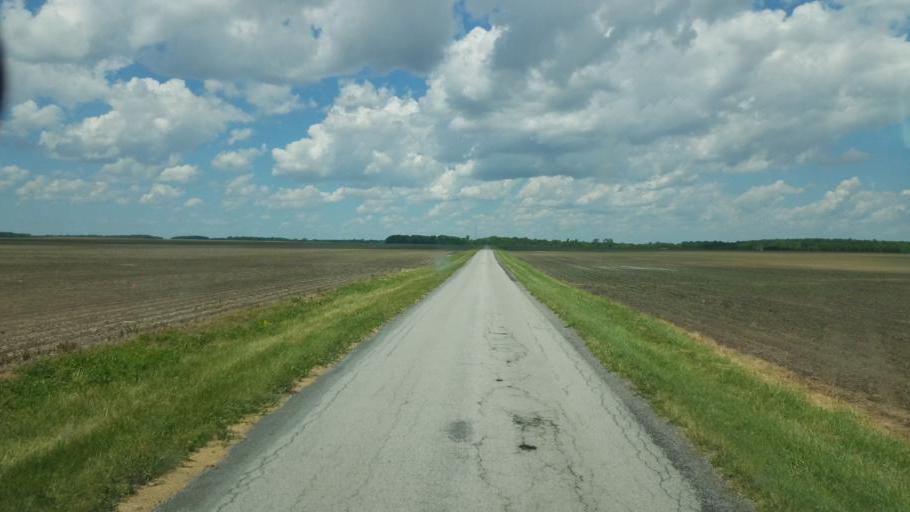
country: US
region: Ohio
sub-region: Wyandot County
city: Upper Sandusky
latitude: 40.7528
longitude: -83.2409
